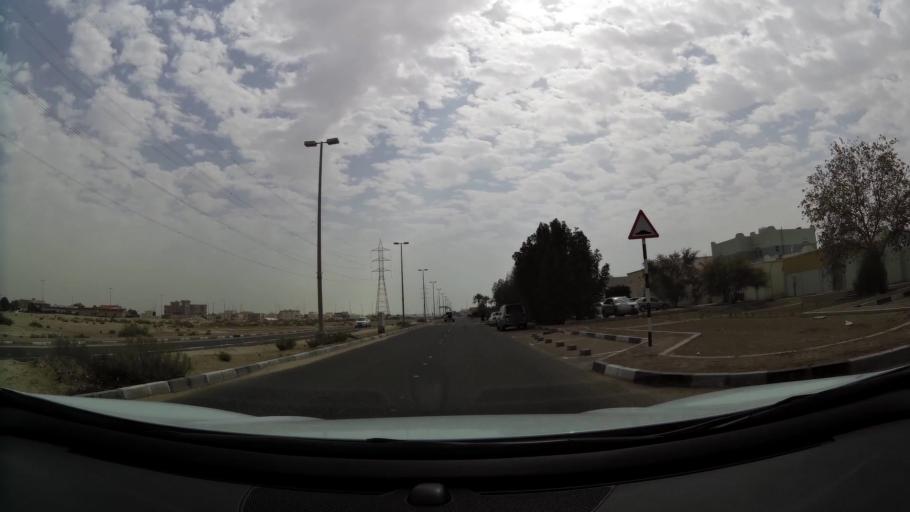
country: AE
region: Abu Dhabi
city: Abu Dhabi
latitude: 24.3120
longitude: 54.6394
